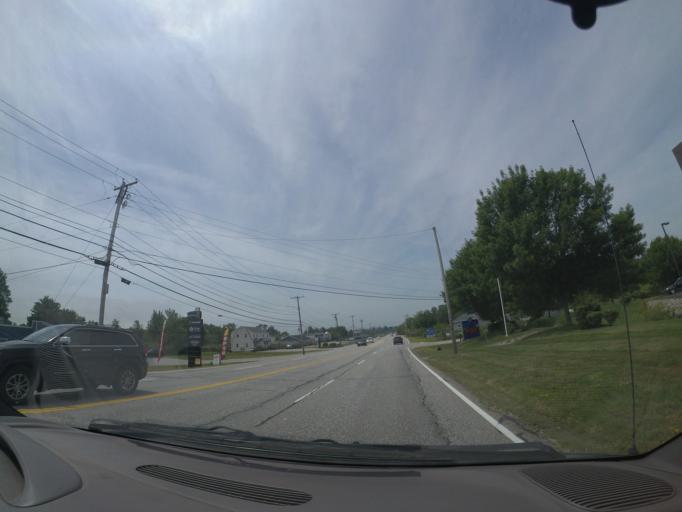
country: US
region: Maine
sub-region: Cumberland County
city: West Scarborough
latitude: 43.5829
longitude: -70.3641
